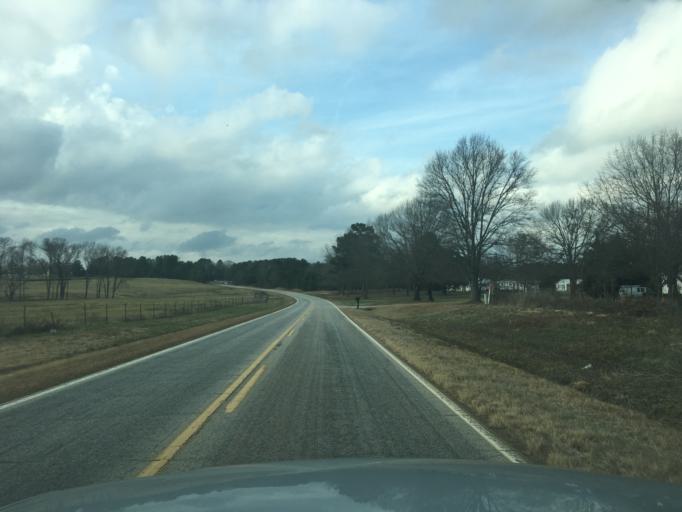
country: US
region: South Carolina
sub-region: Abbeville County
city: Abbeville
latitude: 34.2324
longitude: -82.3929
